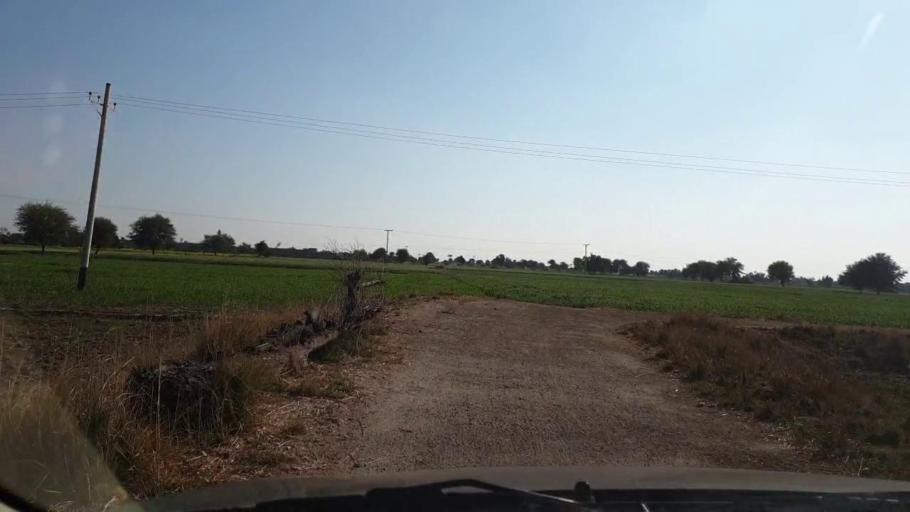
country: PK
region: Sindh
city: Sinjhoro
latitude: 25.9821
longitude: 68.8365
